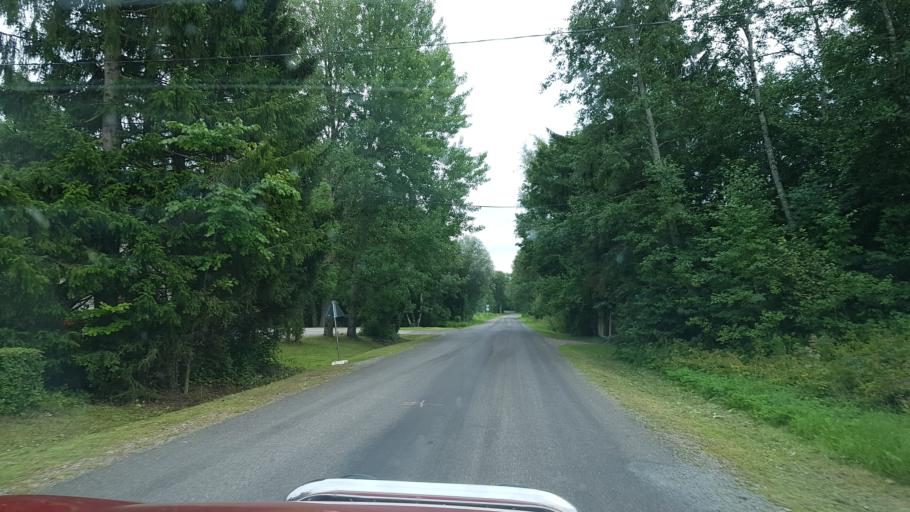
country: EE
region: Laeaene
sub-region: Lihula vald
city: Lihula
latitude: 58.8543
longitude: 23.8017
